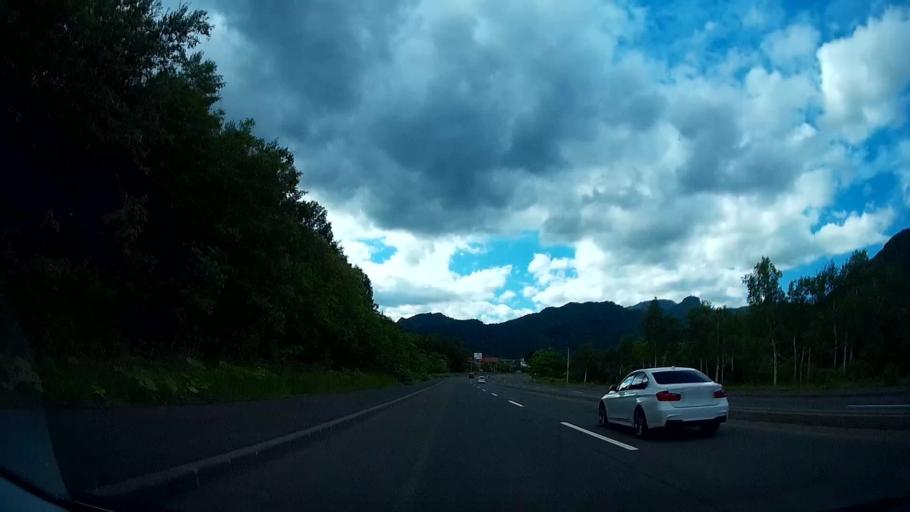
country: JP
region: Hokkaido
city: Sapporo
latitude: 42.9602
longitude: 141.2251
